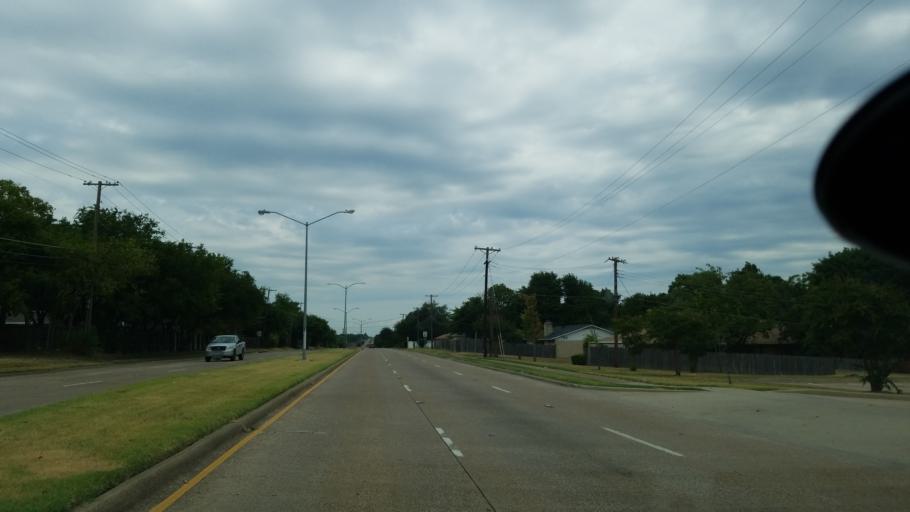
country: US
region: Texas
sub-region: Dallas County
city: Duncanville
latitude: 32.6644
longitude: -96.8400
